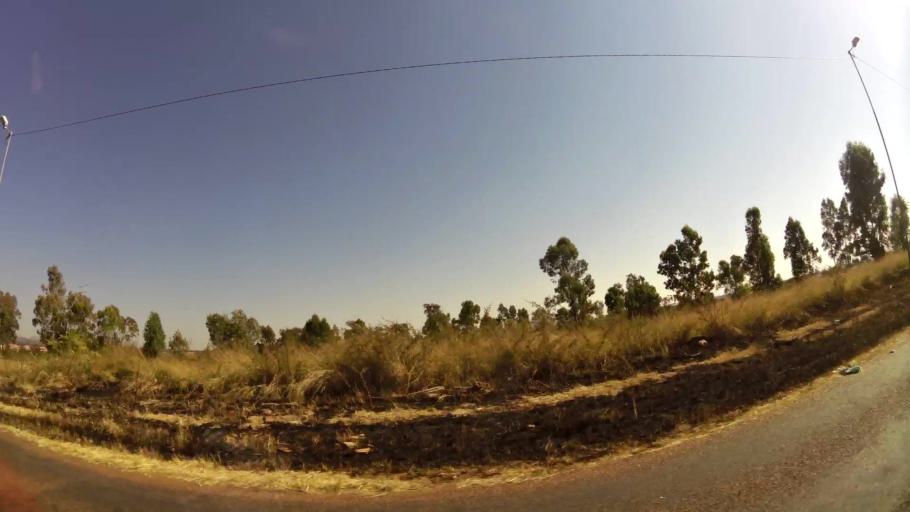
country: ZA
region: North-West
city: Ga-Rankuwa
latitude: -25.6461
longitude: 28.0890
